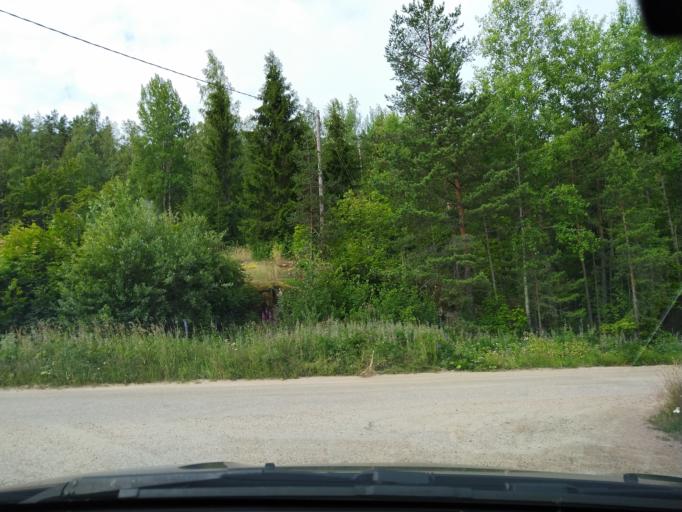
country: FI
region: Kymenlaakso
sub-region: Kouvola
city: Jaala
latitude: 61.0629
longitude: 26.6367
